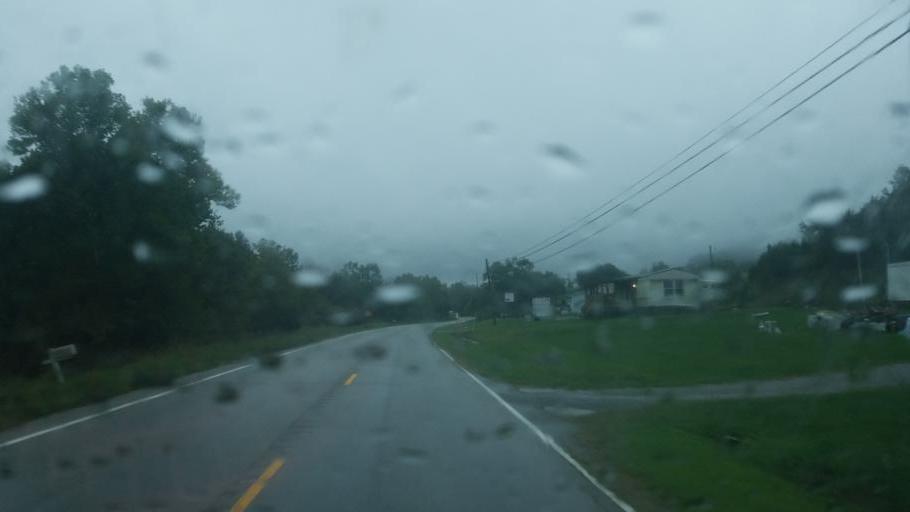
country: US
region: Kentucky
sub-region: Fleming County
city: Flemingsburg
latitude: 38.3748
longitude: -83.6334
